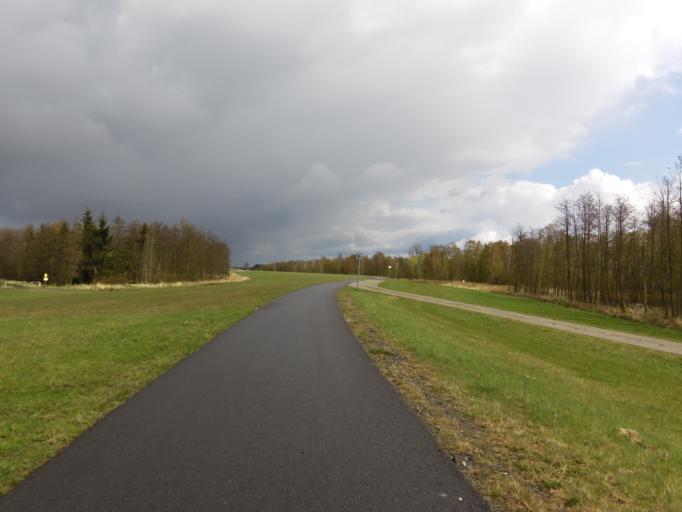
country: DE
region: Mecklenburg-Vorpommern
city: Altenpleen
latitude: 54.4316
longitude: 12.8911
